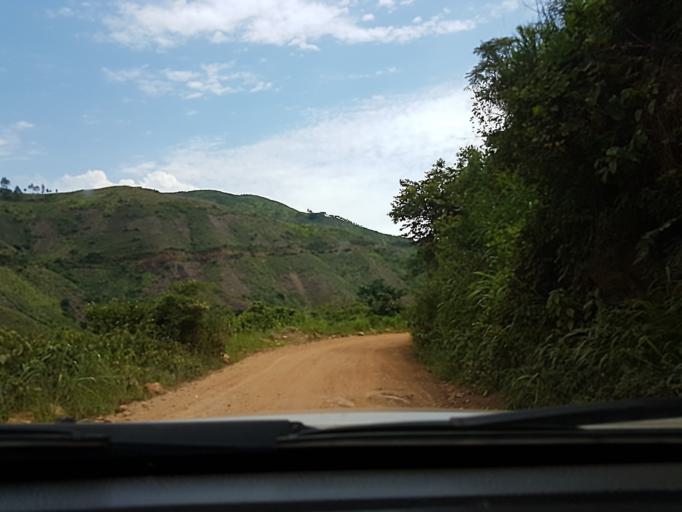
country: RW
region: Western Province
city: Cyangugu
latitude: -2.7088
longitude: 28.9445
